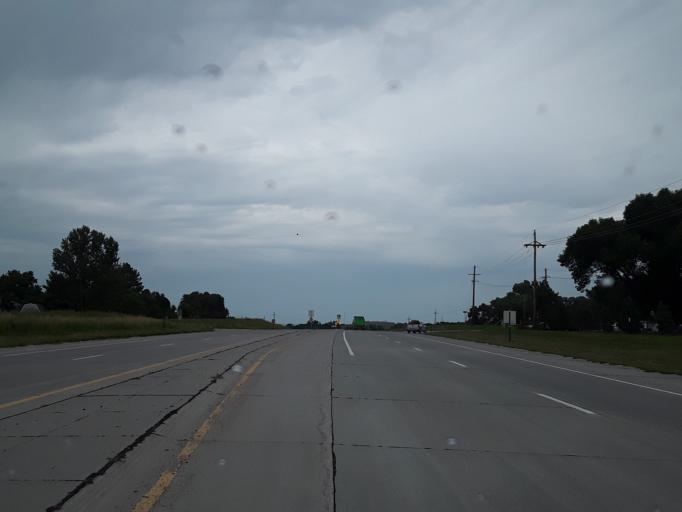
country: US
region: Nebraska
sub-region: Washington County
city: Blair
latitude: 41.5007
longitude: -96.1474
